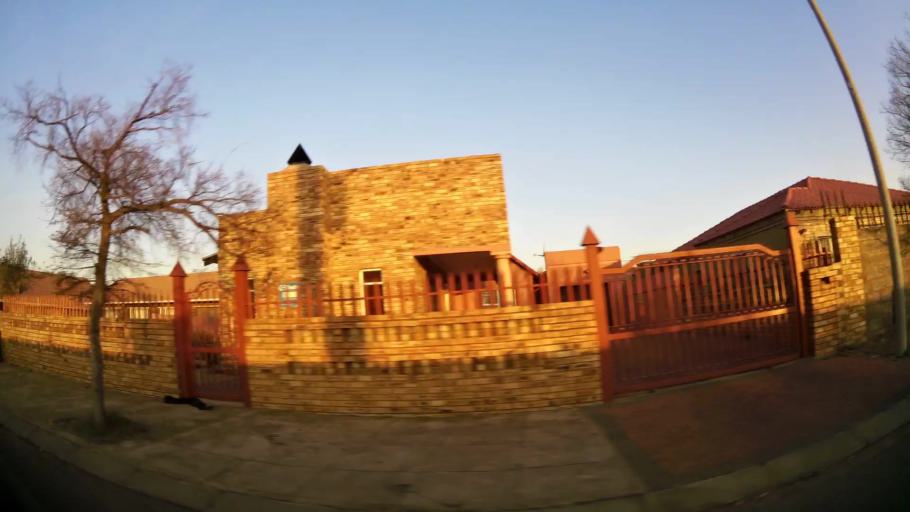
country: ZA
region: Gauteng
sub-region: West Rand District Municipality
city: Randfontein
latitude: -26.2020
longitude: 27.7048
